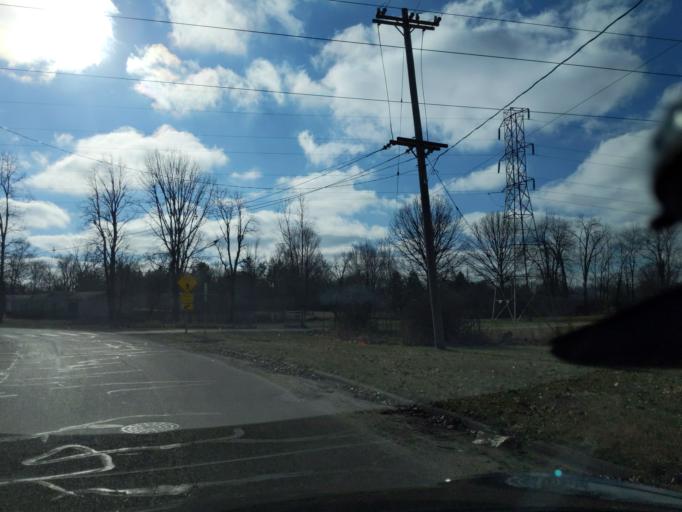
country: US
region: Michigan
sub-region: Ingham County
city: Lansing
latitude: 42.6772
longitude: -84.5790
